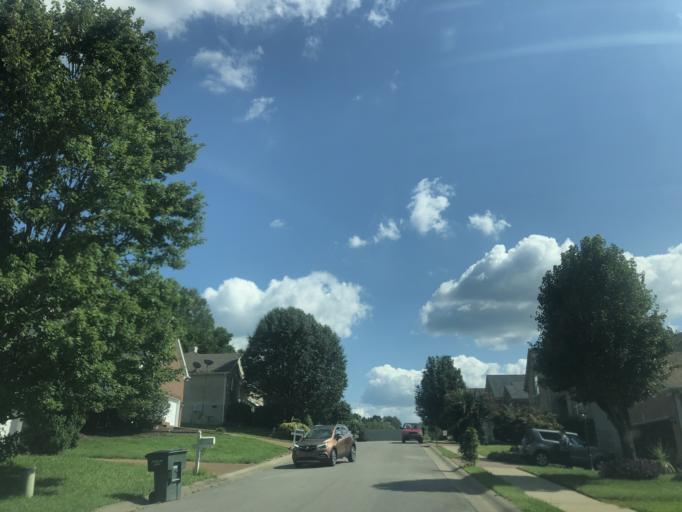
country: US
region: Tennessee
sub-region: Davidson County
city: Lakewood
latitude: 36.1902
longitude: -86.6046
